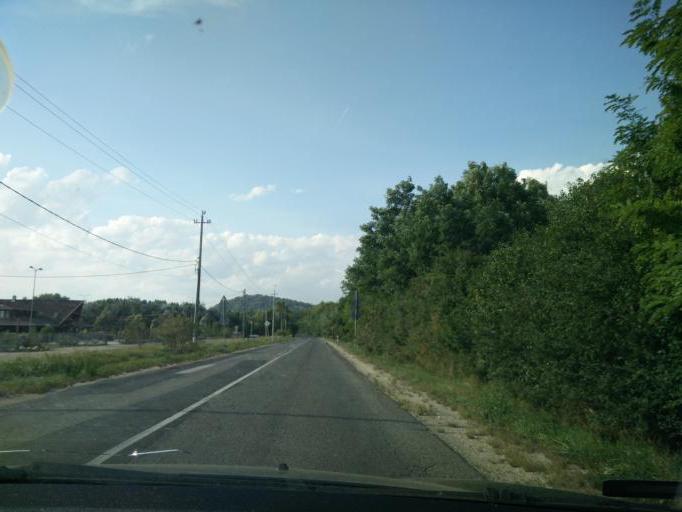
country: HU
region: Pest
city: Piliscsaba
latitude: 47.6467
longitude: 18.8057
